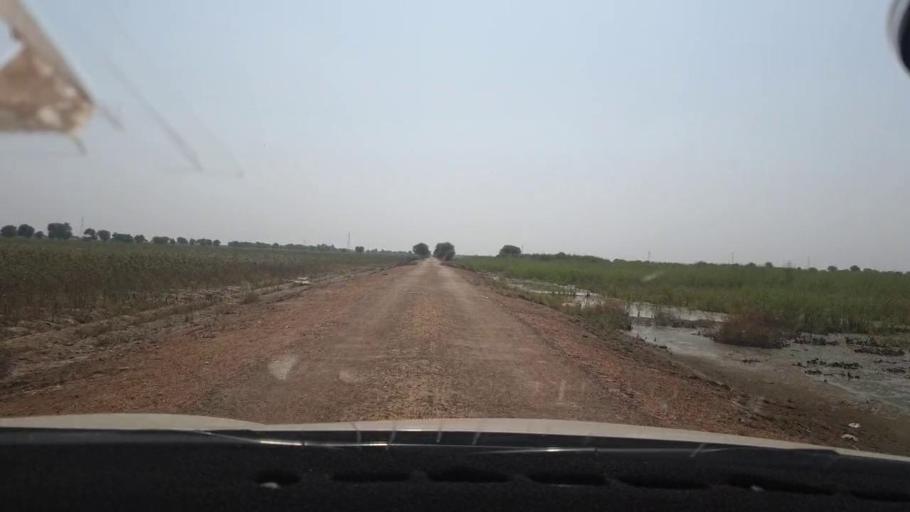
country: PK
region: Sindh
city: Tando Mittha Khan
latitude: 25.9119
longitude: 69.2066
